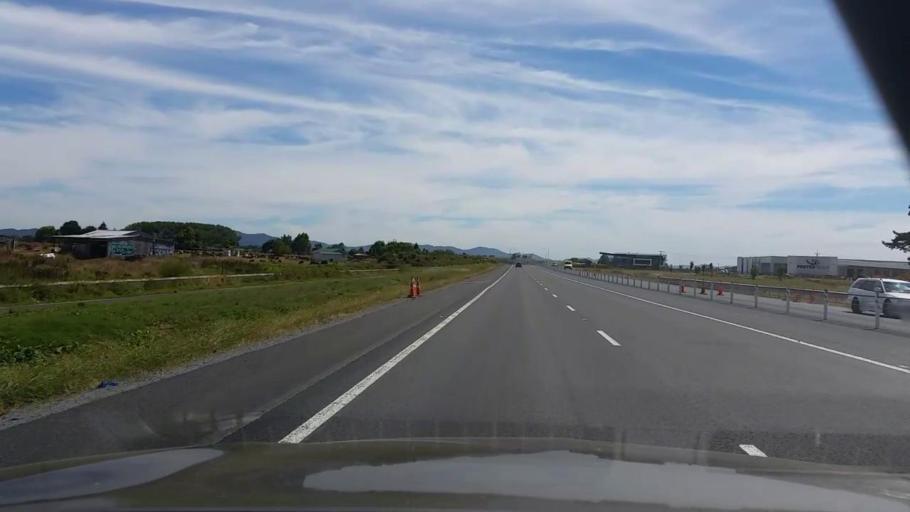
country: NZ
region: Waikato
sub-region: Hamilton City
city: Hamilton
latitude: -37.7451
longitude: 175.2145
